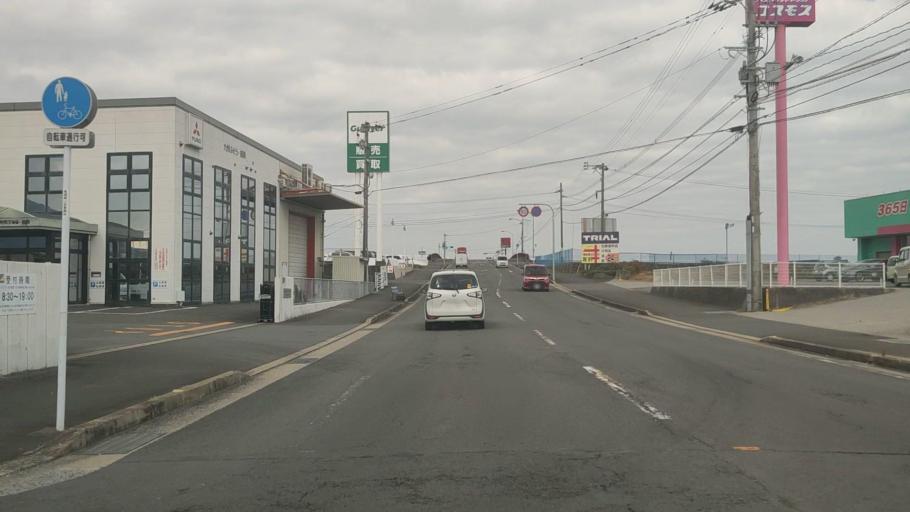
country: JP
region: Nagasaki
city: Shimabara
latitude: 32.8065
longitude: 130.3616
